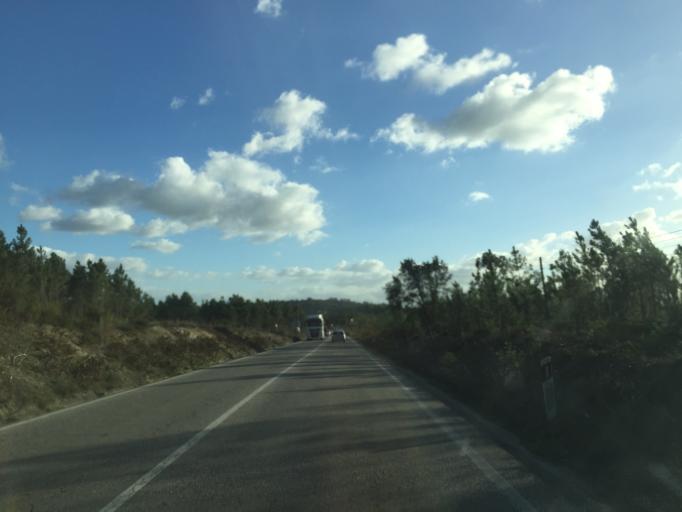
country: PT
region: Leiria
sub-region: Leiria
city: Monte Redondo
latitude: 39.8734
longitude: -8.8389
